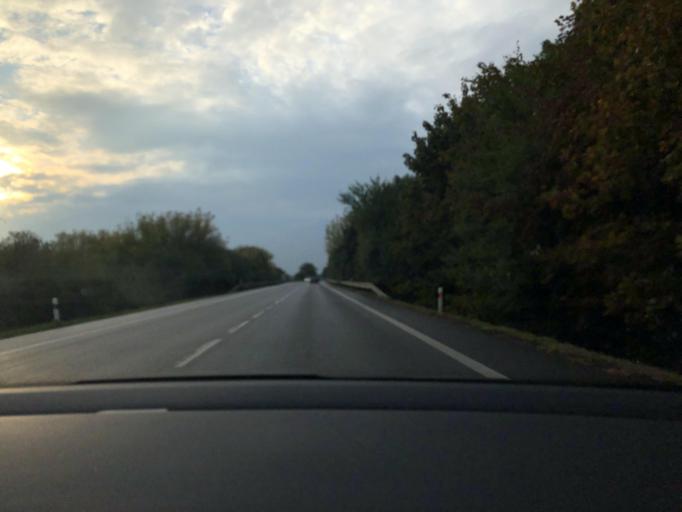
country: CZ
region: Central Bohemia
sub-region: Okres Kolin
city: Kolin
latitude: 50.0338
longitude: 15.1608
